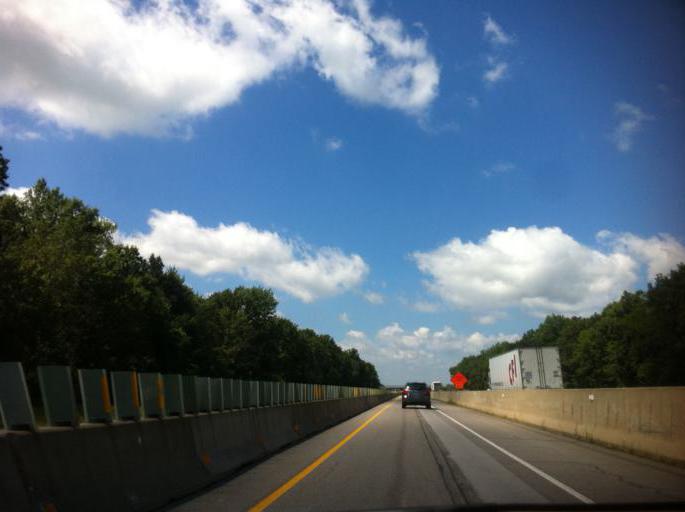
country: US
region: Ohio
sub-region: Sandusky County
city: Clyde
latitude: 41.3592
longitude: -82.9076
